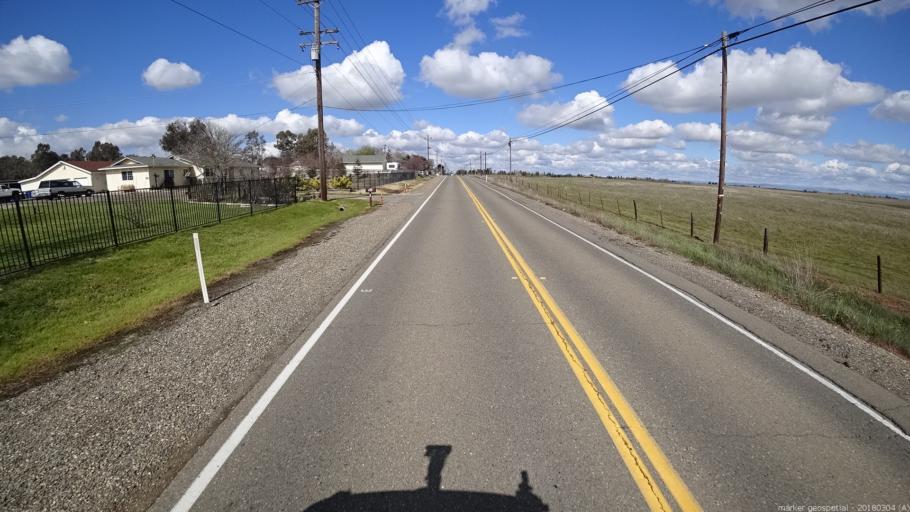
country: US
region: California
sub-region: Sacramento County
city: Vineyard
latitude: 38.4735
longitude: -121.2977
